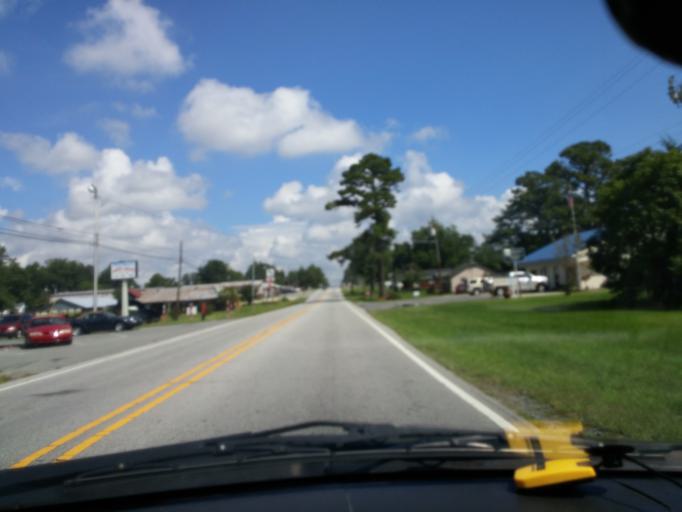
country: US
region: North Carolina
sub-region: Duplin County
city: Beulaville
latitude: 35.0612
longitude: -77.7404
